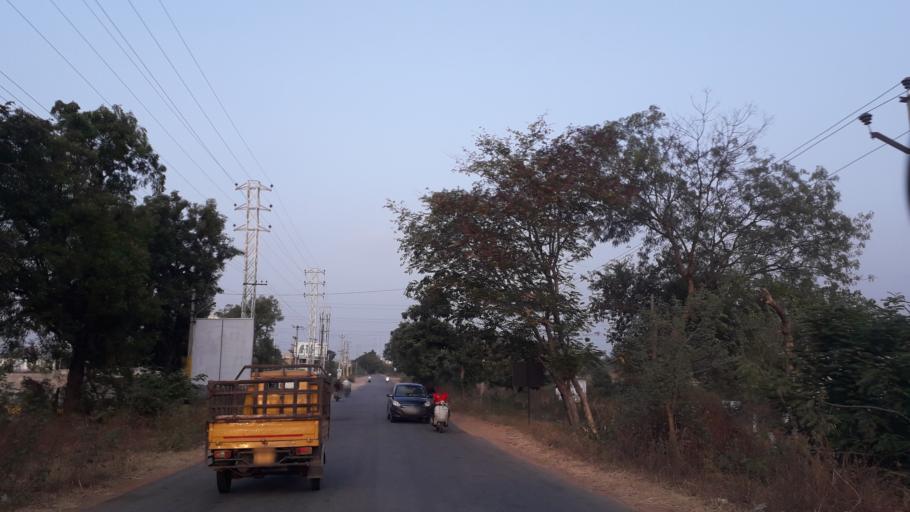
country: IN
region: Telangana
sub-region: Rangareddi
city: Singapur
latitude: 17.4825
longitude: 78.1716
